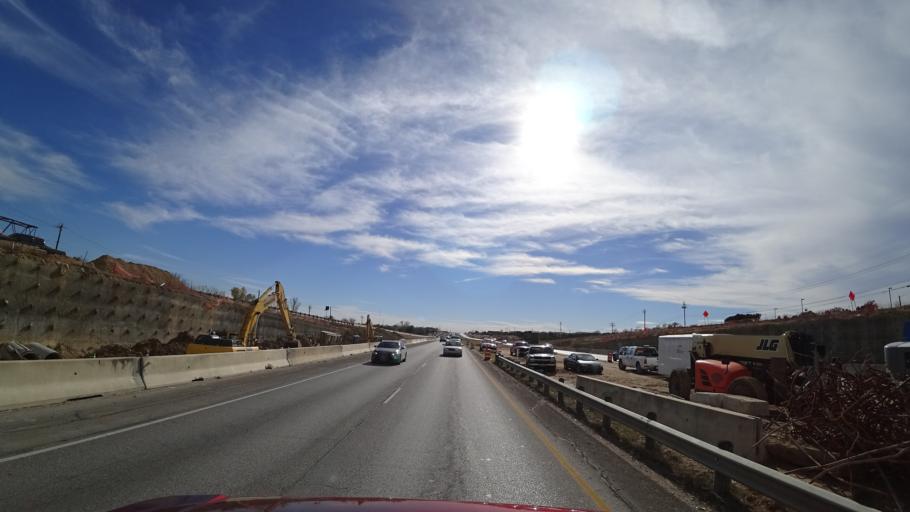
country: US
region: Texas
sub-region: Travis County
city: Austin
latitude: 30.2851
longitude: -97.6654
